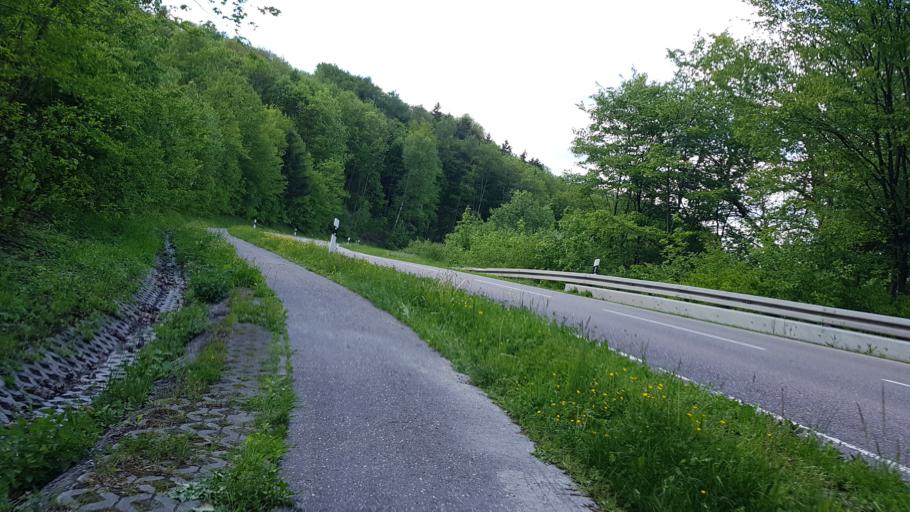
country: DE
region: Baden-Wuerttemberg
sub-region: Regierungsbezirk Stuttgart
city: Kirchberg an der Murr
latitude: 48.9356
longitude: 9.3332
